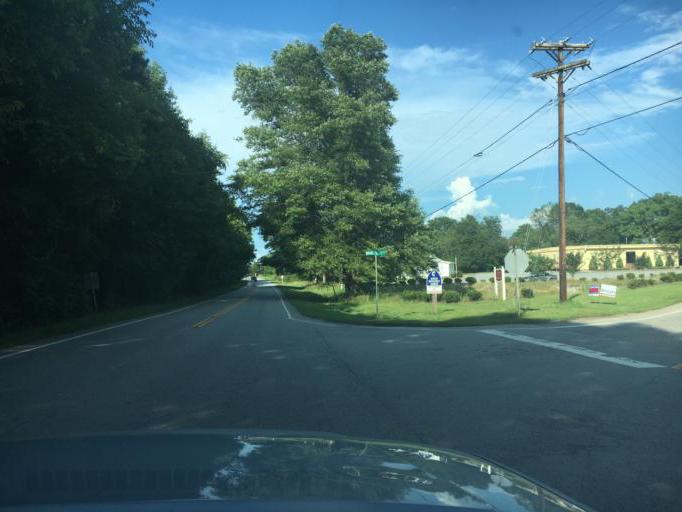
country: US
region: South Carolina
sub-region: Greenville County
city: Mauldin
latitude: 34.7779
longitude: -82.2806
